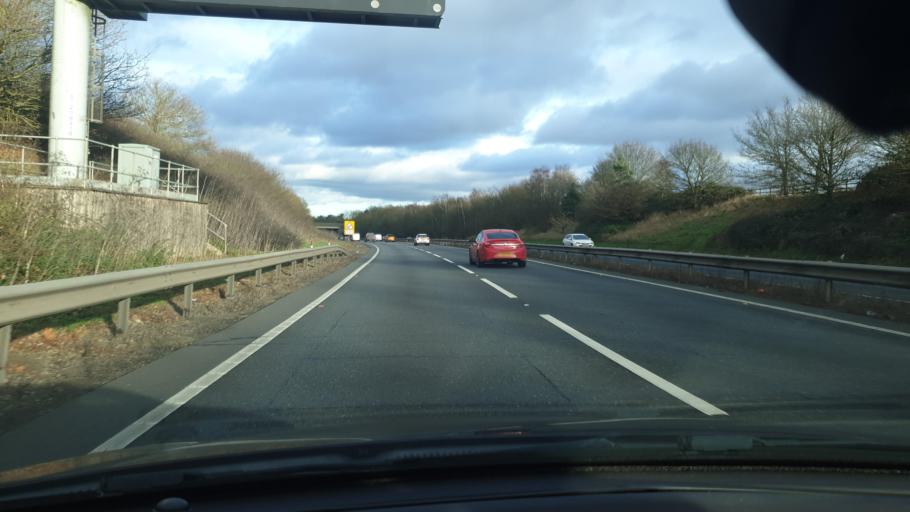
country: GB
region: England
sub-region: Suffolk
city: Bramford
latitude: 52.0261
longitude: 1.0904
